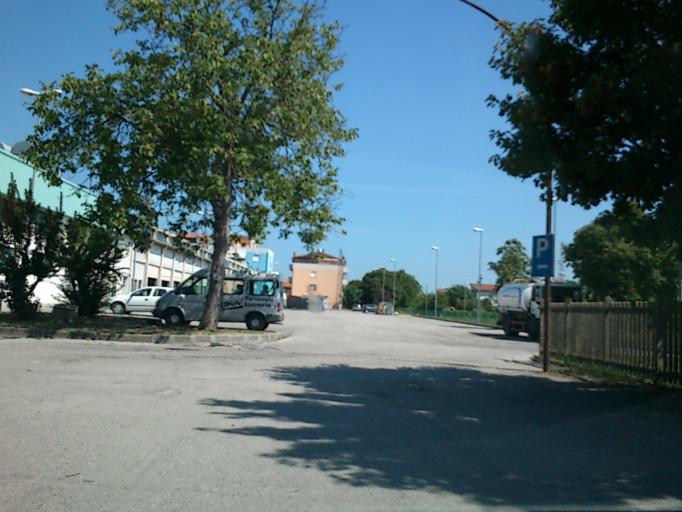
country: IT
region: The Marches
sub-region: Provincia di Pesaro e Urbino
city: Lucrezia
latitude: 43.7711
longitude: 12.9378
